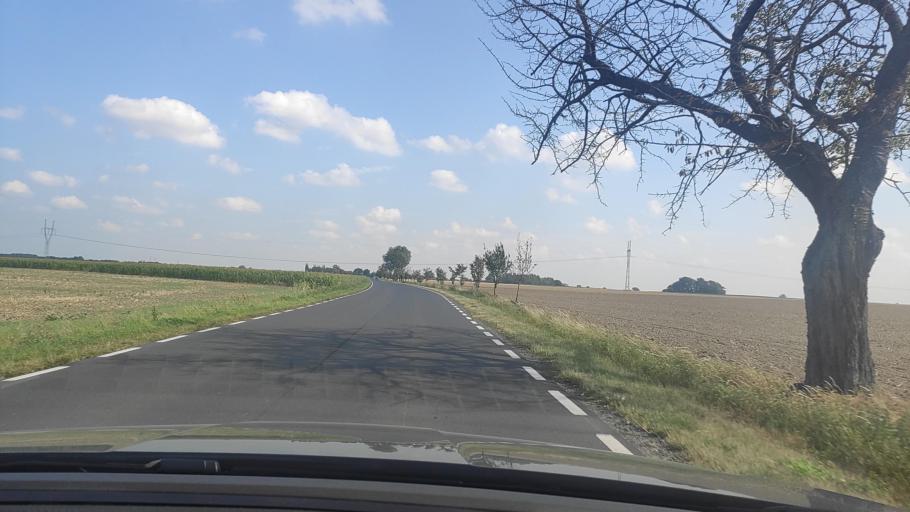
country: PL
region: Greater Poland Voivodeship
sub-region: Powiat poznanski
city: Kostrzyn
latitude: 52.4341
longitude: 17.1623
